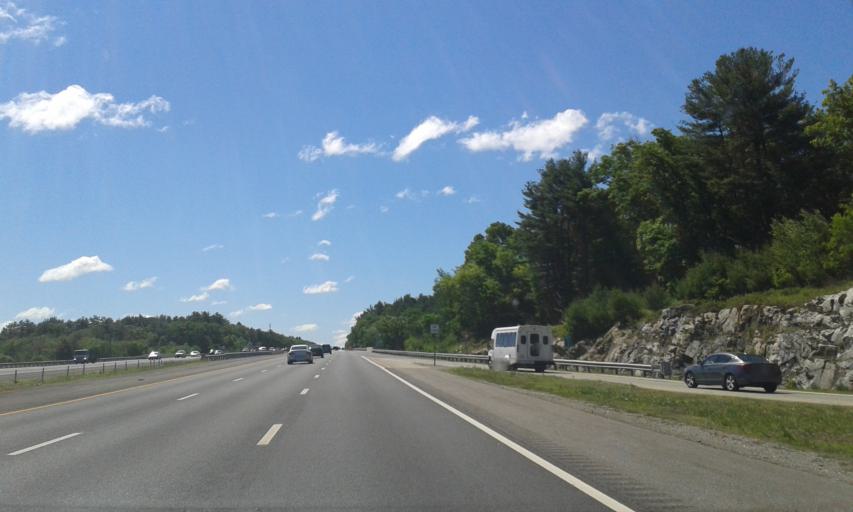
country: US
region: Massachusetts
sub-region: Middlesex County
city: Pinehurst
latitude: 42.5041
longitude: -71.2456
